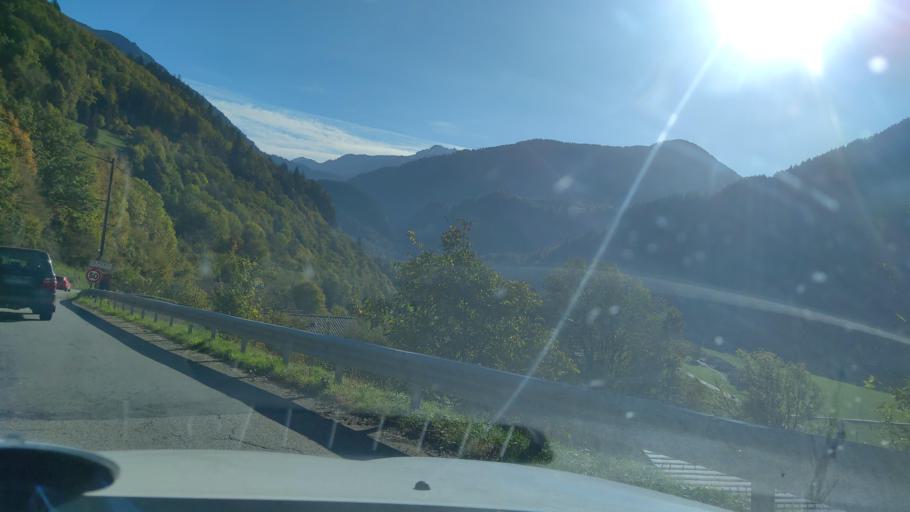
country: FR
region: Rhone-Alpes
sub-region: Departement de la Savoie
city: Beaufort
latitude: 45.7277
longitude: 6.5513
